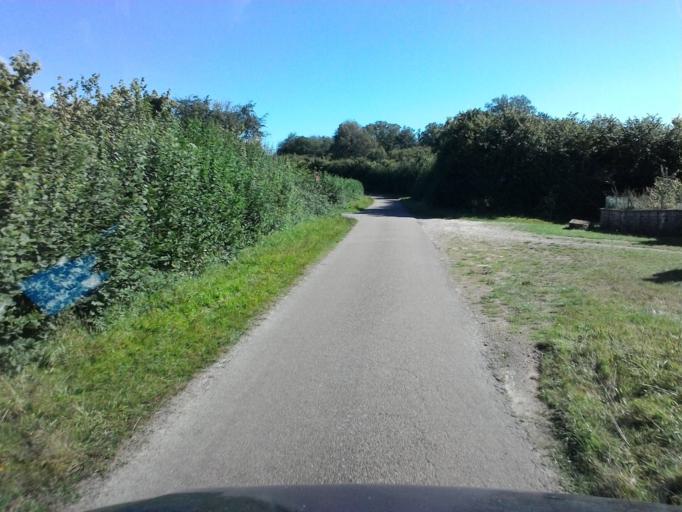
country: FR
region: Bourgogne
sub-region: Departement de la Cote-d'Or
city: Saulieu
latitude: 47.2494
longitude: 4.2176
